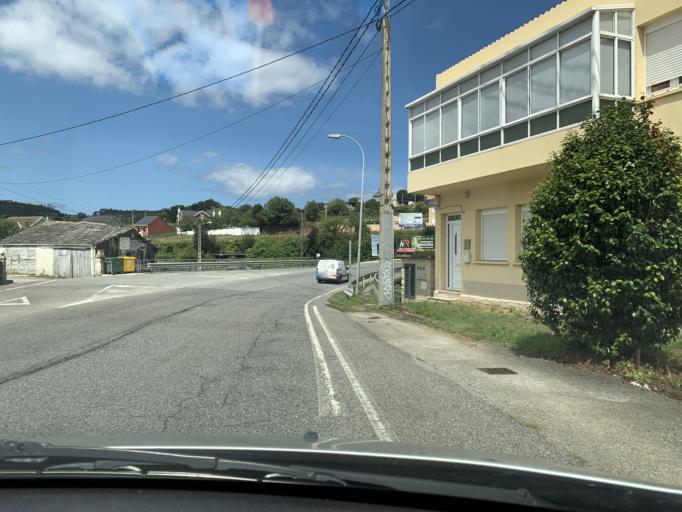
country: ES
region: Galicia
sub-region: Provincia de Lugo
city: Foz
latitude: 43.5627
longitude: -7.2718
